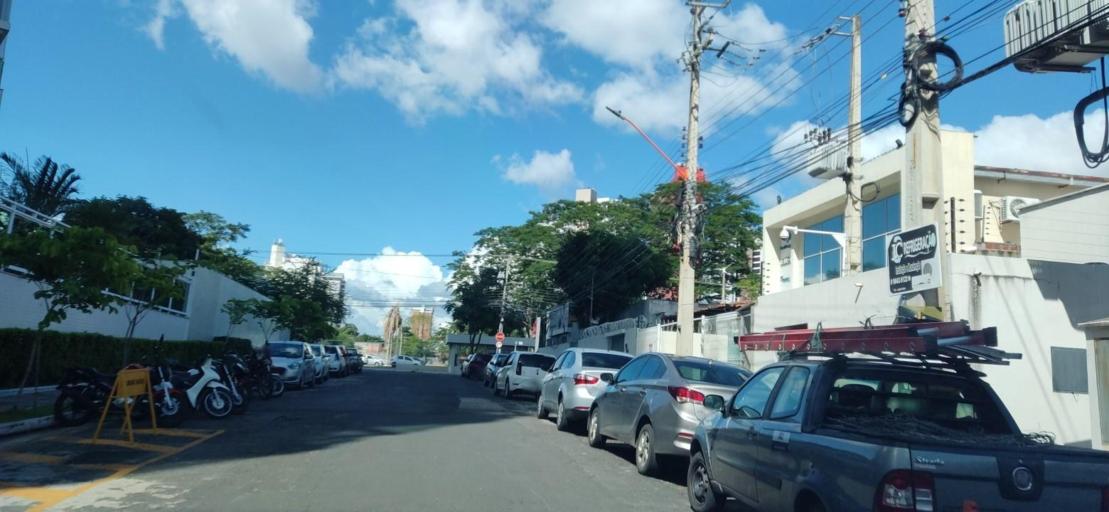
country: BR
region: Piaui
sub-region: Teresina
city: Teresina
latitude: -5.0775
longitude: -42.7910
